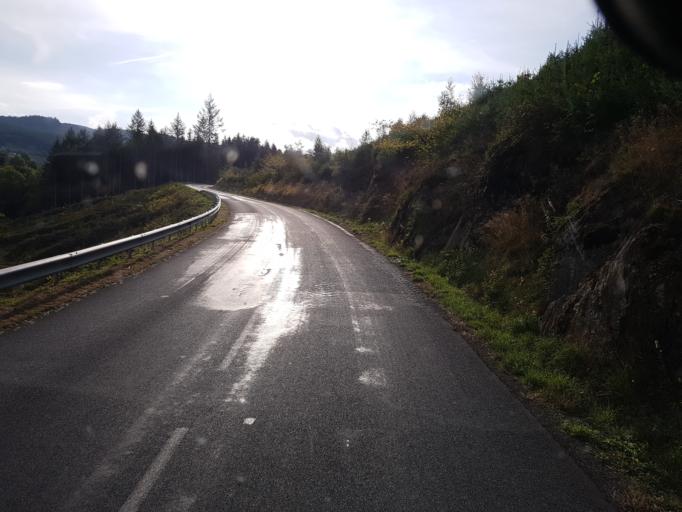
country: FR
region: Bourgogne
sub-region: Departement de Saone-et-Loire
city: Chauffailles
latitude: 46.2103
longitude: 4.4359
